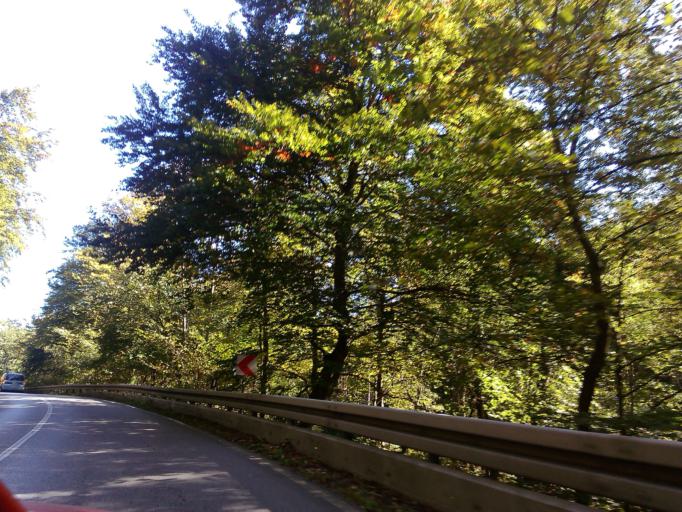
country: DE
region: Bavaria
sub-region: Upper Bavaria
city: Starnberg
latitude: 48.0299
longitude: 11.3609
